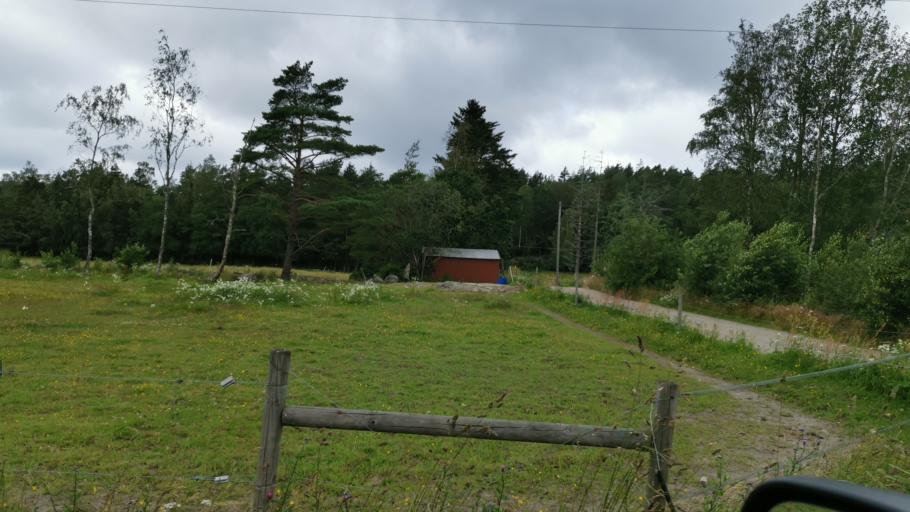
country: SE
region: Vaestra Goetaland
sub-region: Orust
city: Henan
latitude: 58.2916
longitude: 11.6026
